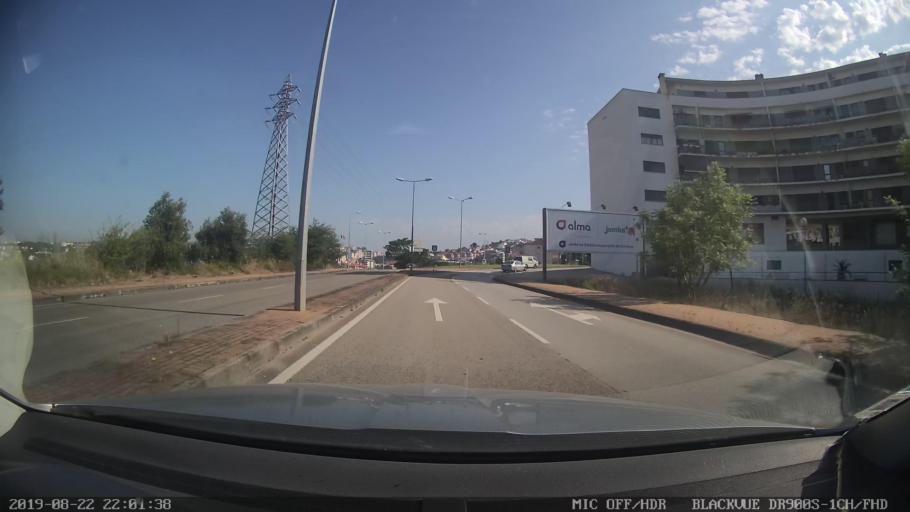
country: PT
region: Coimbra
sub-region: Coimbra
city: Coimbra
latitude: 40.1931
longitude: -8.3988
